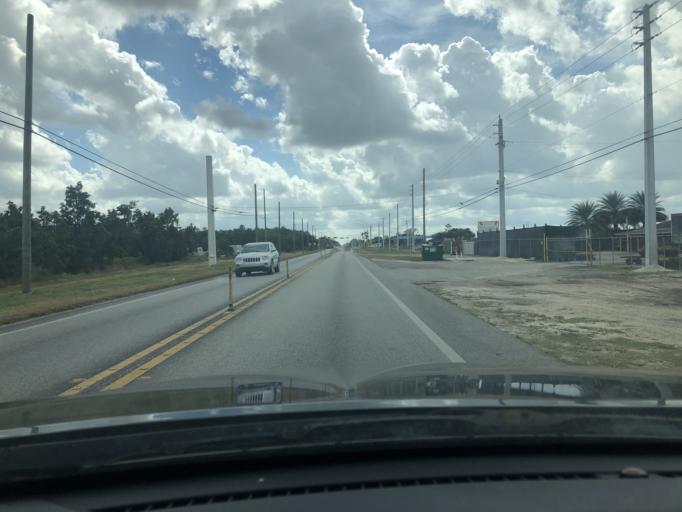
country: US
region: Florida
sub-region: Miami-Dade County
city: Homestead
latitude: 25.5240
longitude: -80.4779
